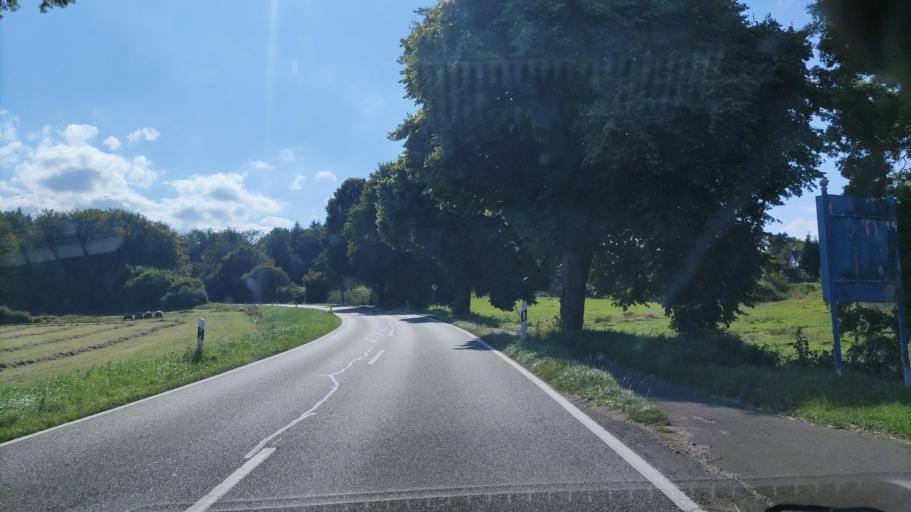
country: DE
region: Schleswig-Holstein
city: Ascheffel
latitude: 54.4297
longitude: 9.7074
